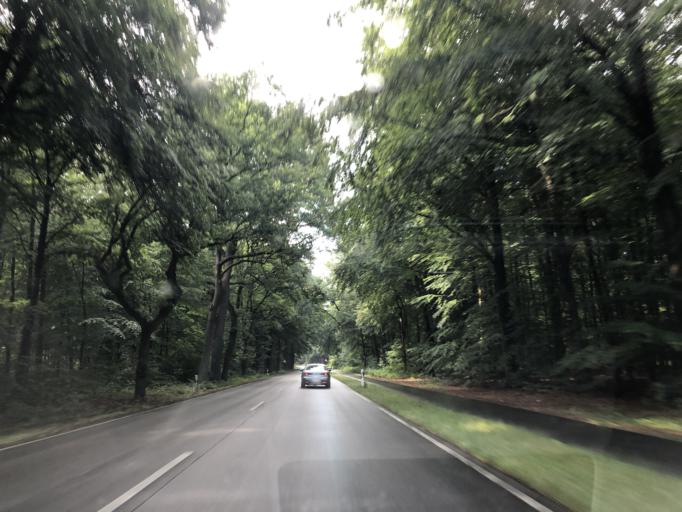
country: DE
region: North Rhine-Westphalia
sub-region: Regierungsbezirk Dusseldorf
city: Kranenburg
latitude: 51.7391
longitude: 6.0362
